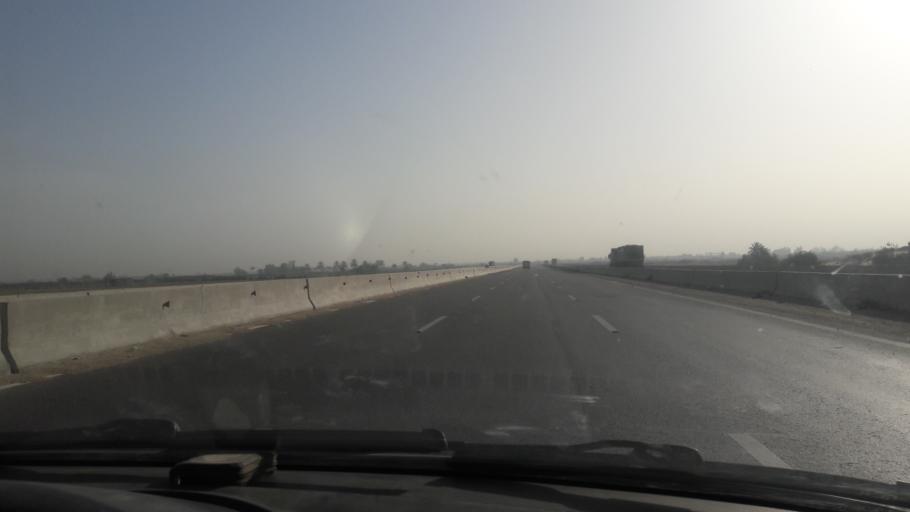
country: EG
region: Al Isma'iliyah
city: Ismailia
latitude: 30.7680
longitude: 32.1413
